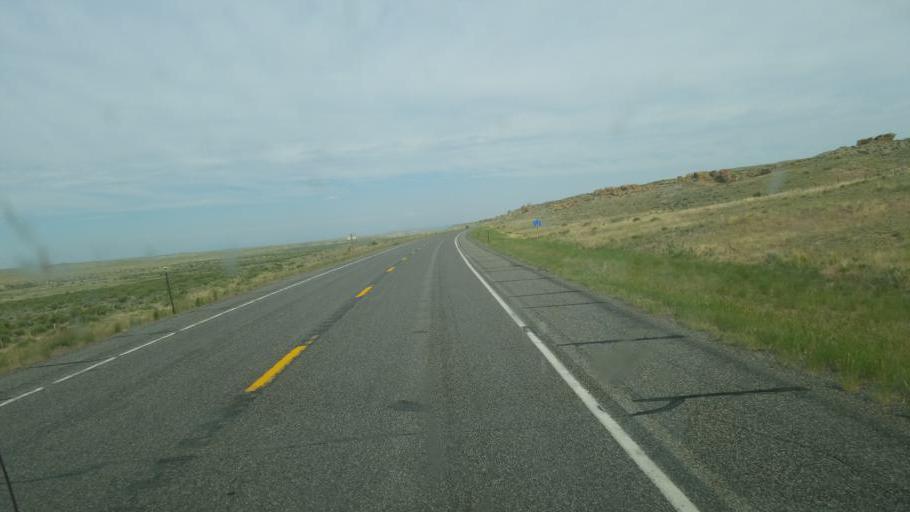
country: US
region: Wyoming
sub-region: Fremont County
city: Riverton
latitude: 43.2207
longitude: -108.0147
